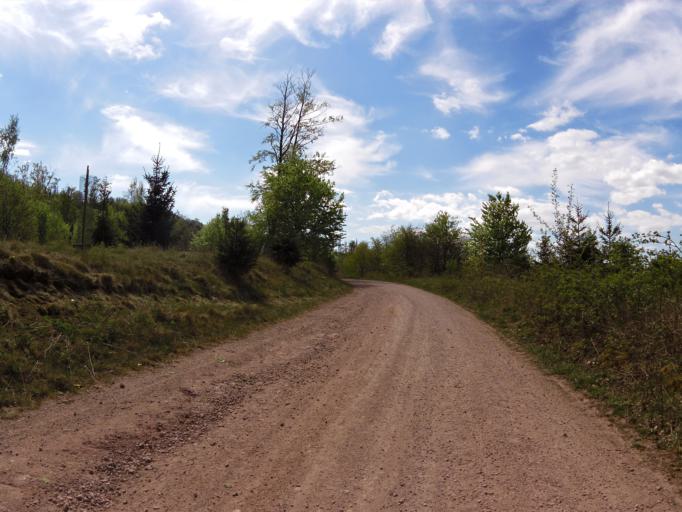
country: DE
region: Thuringia
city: Ruhla
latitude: 50.9150
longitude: 10.3314
